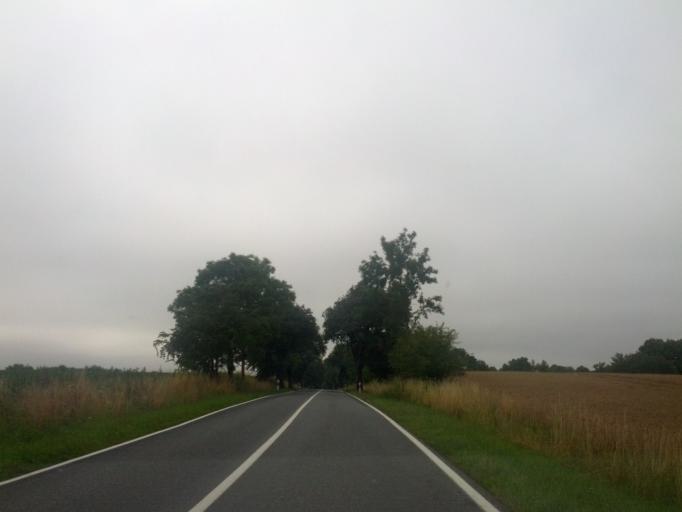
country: DE
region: Mecklenburg-Vorpommern
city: Biendorf
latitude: 54.0830
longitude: 11.6787
